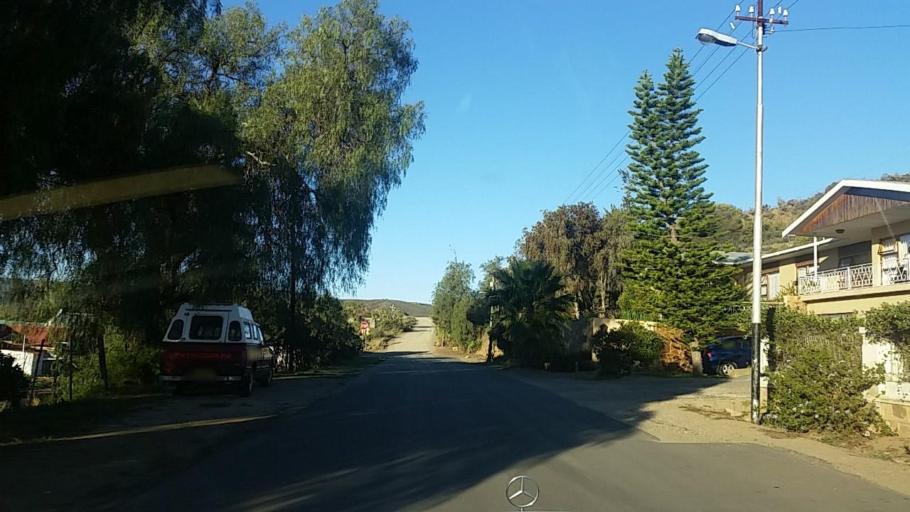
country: ZA
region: Western Cape
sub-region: Eden District Municipality
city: Knysna
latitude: -33.6568
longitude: 23.1289
